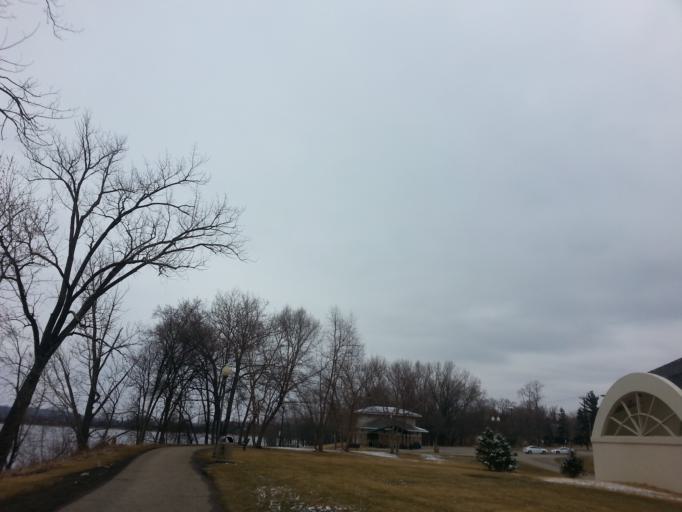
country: US
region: Wisconsin
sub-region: Saint Croix County
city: Hudson
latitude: 44.9756
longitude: -92.7597
